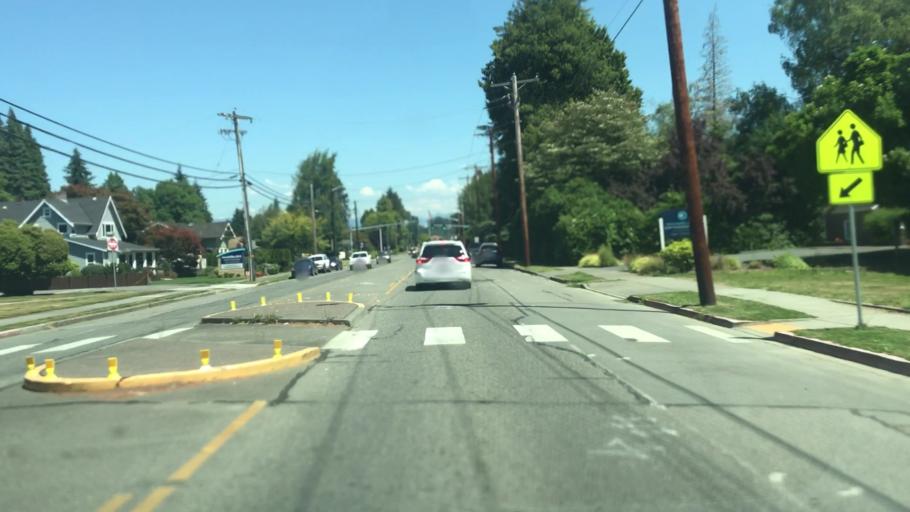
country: US
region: Washington
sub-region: Snohomish County
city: Monroe
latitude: 47.8531
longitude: -121.9792
